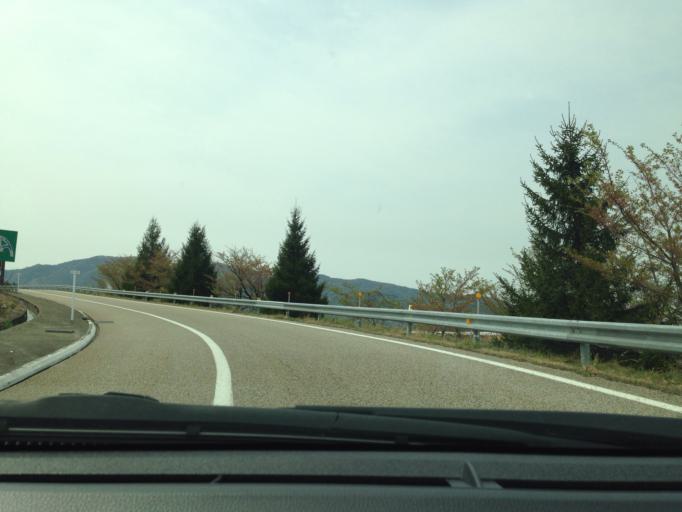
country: JP
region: Toyama
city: Fukumitsu
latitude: 36.5043
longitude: 136.8740
